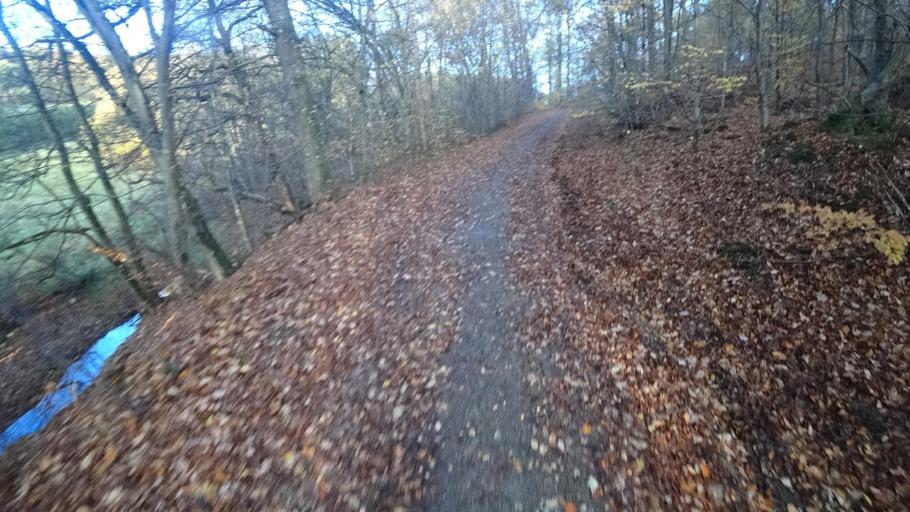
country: DE
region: Rheinland-Pfalz
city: Berg
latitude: 50.5476
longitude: 6.9621
